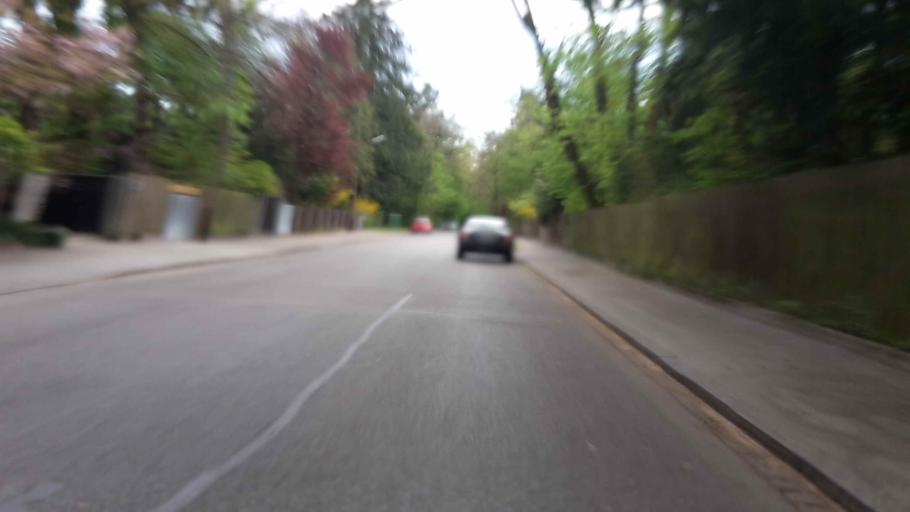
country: DE
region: Bavaria
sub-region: Upper Bavaria
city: Pasing
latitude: 48.1708
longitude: 11.4884
